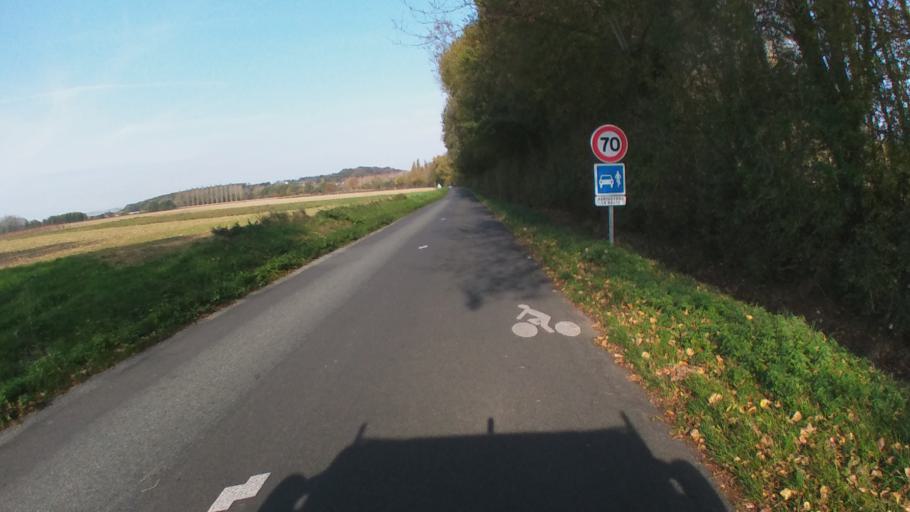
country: FR
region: Pays de la Loire
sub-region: Departement de Maine-et-Loire
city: Chace
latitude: 47.2155
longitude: -0.0907
